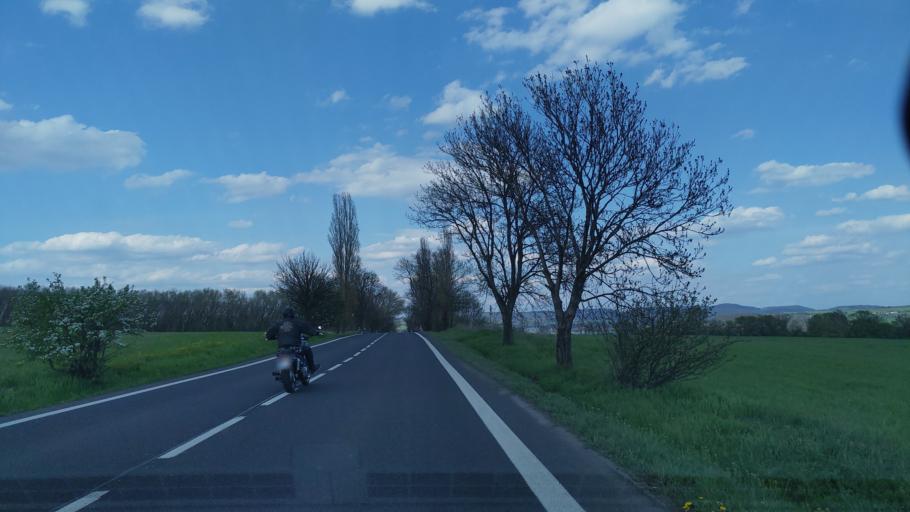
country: CZ
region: Ustecky
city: Chabarovice
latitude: 50.6772
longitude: 13.9034
